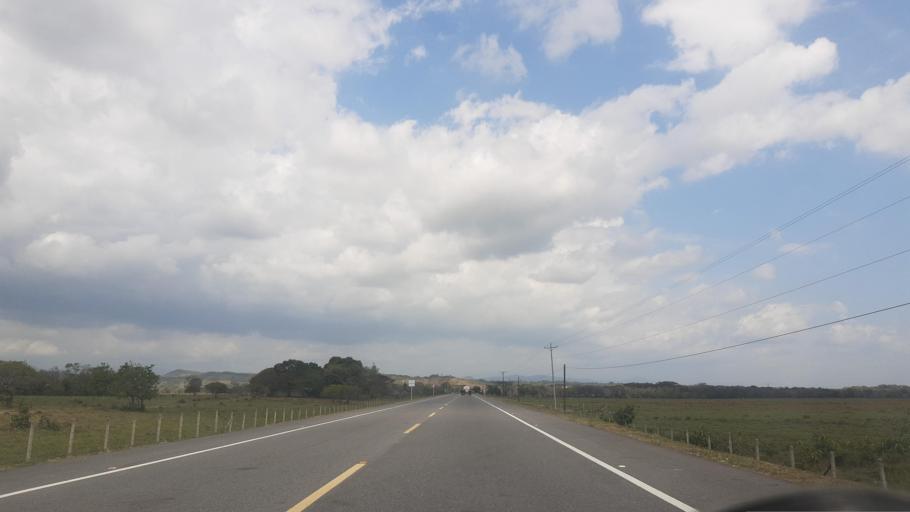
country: CO
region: Casanare
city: Tauramena
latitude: 4.9100
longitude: -72.6758
